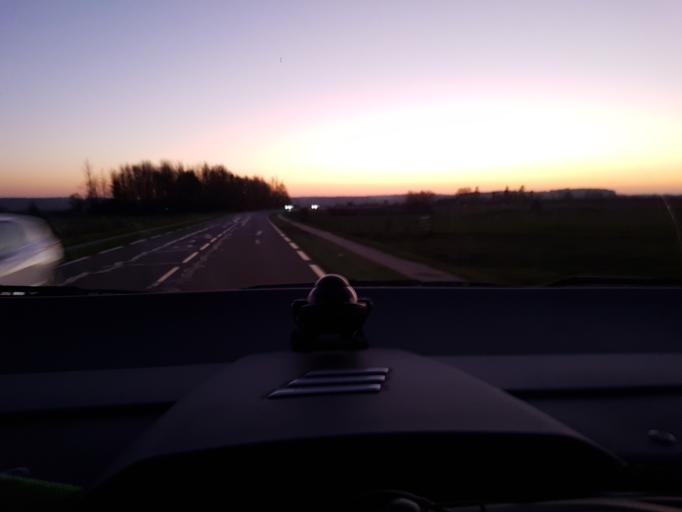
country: FR
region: Picardie
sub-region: Departement de la Somme
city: Saint-Valery-sur-Somme
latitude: 50.1768
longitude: 1.6882
